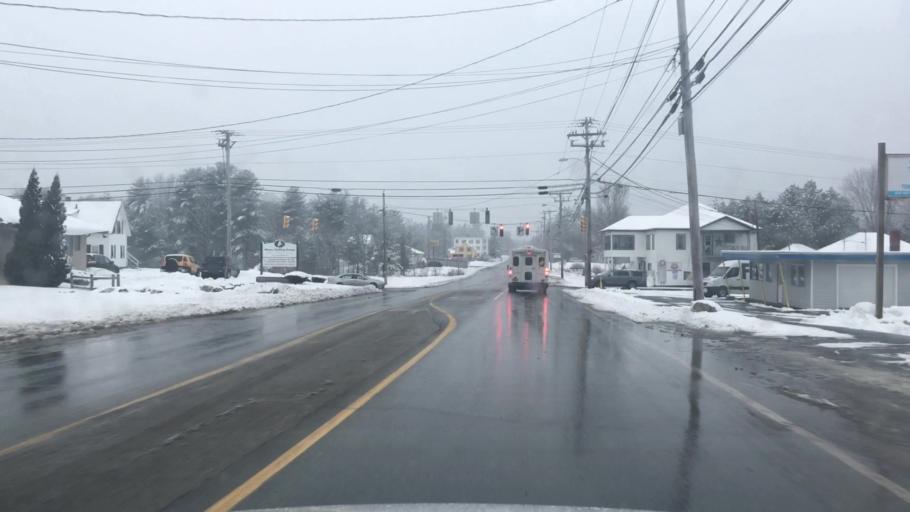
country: US
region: Maine
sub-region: Kennebec County
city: Augusta
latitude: 44.3037
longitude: -69.7417
